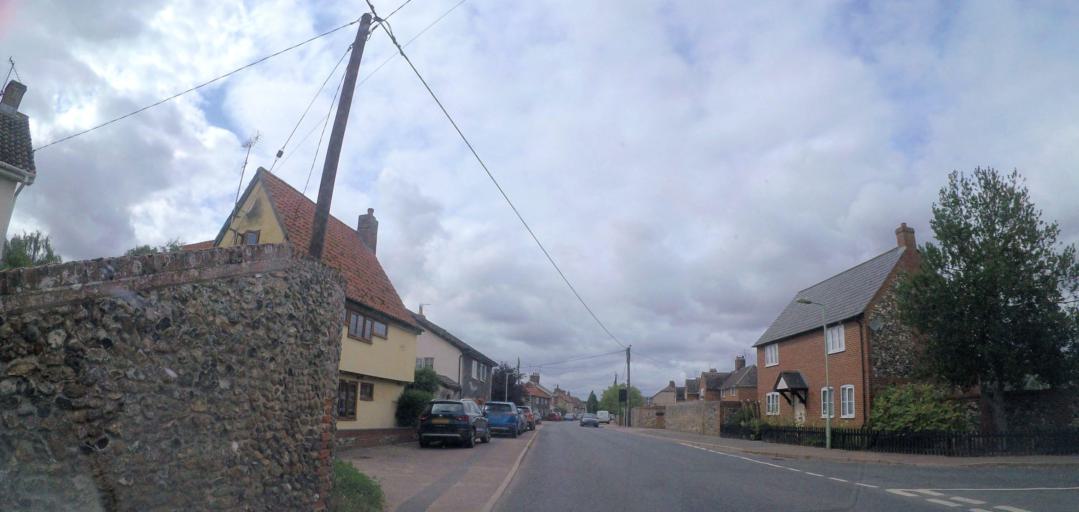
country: GB
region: England
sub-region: Suffolk
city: Lakenheath
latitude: 52.3144
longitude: 0.5460
